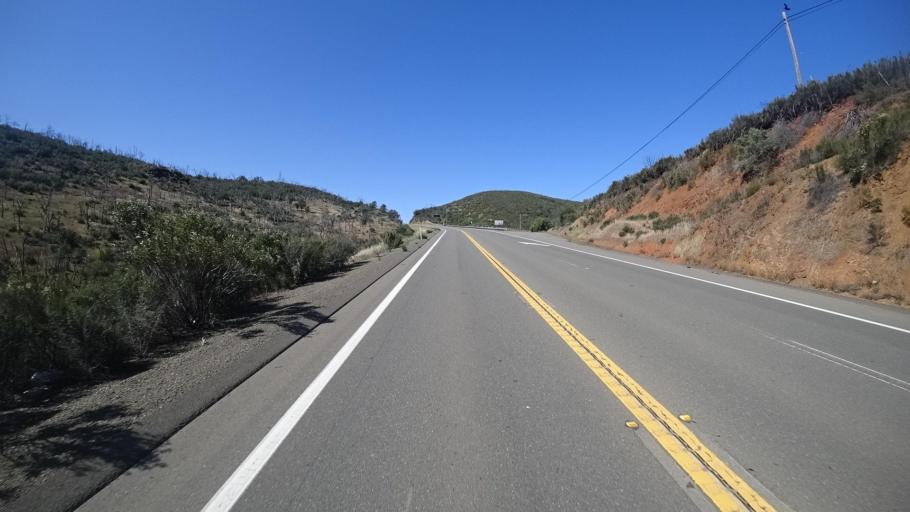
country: US
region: California
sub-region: Lake County
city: Clearlake
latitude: 39.0143
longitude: -122.6021
